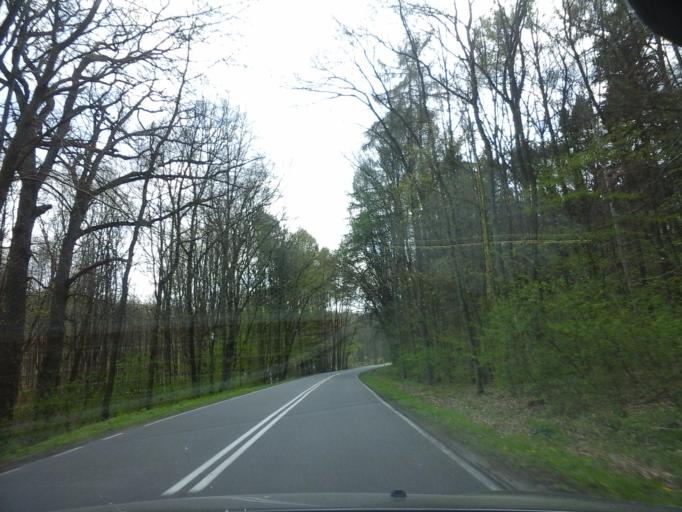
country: PL
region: West Pomeranian Voivodeship
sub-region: Powiat stargardzki
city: Suchan
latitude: 53.2721
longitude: 15.3283
